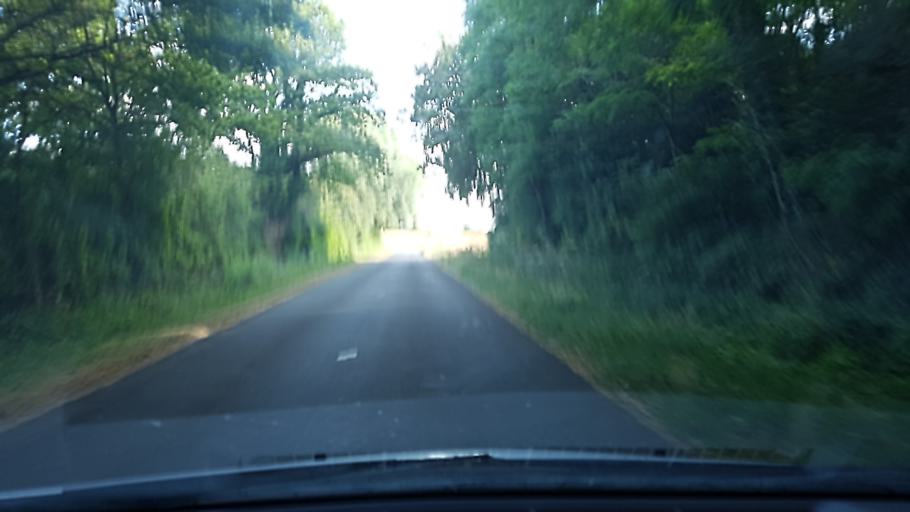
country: FR
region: Pays de la Loire
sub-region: Departement de Maine-et-Loire
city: Jarze
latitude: 47.5165
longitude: -0.2158
